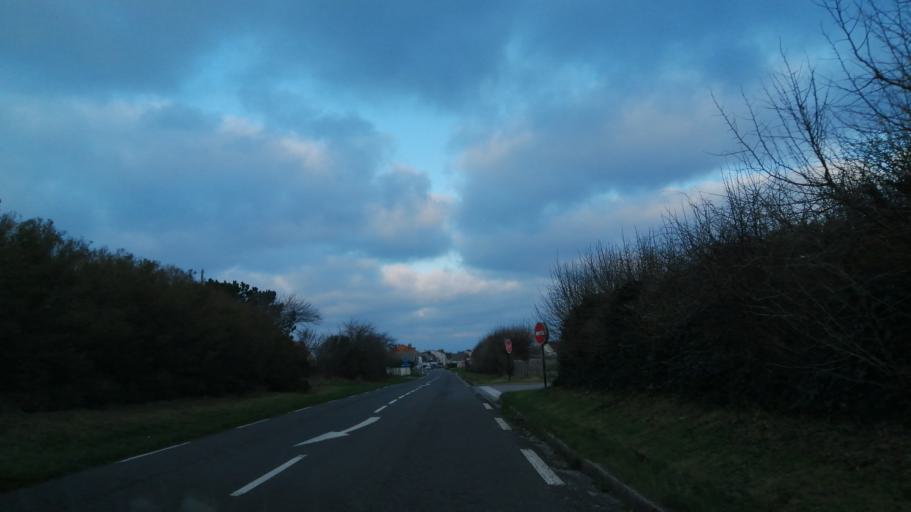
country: FR
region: Nord-Pas-de-Calais
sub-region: Departement du Pas-de-Calais
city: Sangatte
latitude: 50.9406
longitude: 1.7394
